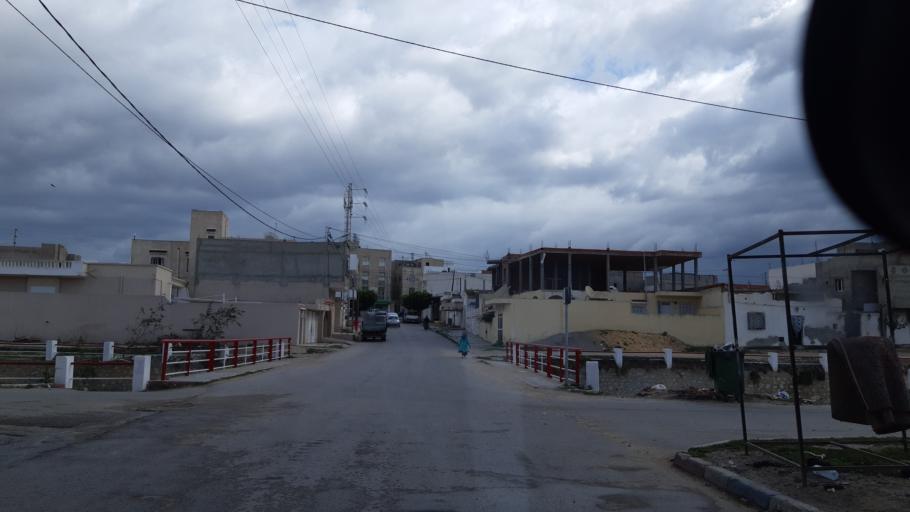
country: TN
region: Susah
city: Akouda
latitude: 35.8742
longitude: 10.5421
